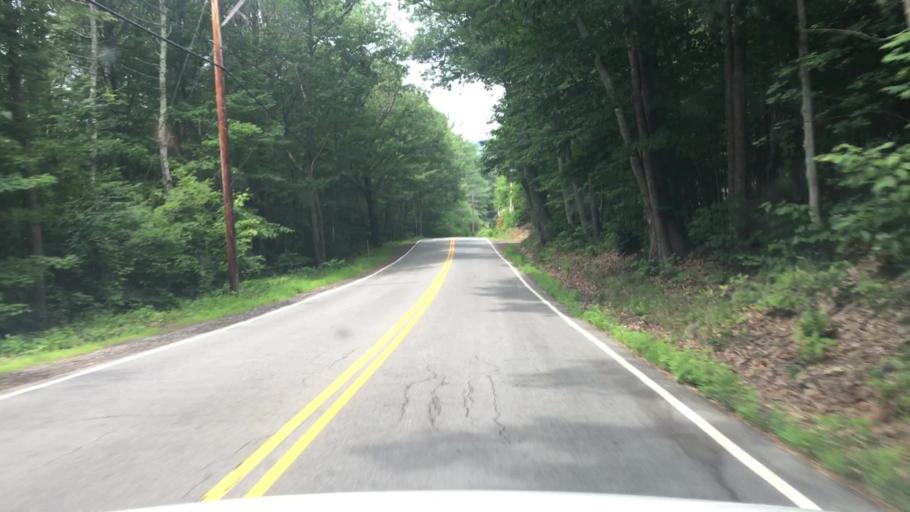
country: US
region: New Hampshire
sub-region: Grafton County
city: Rumney
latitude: 43.7992
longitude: -71.7977
